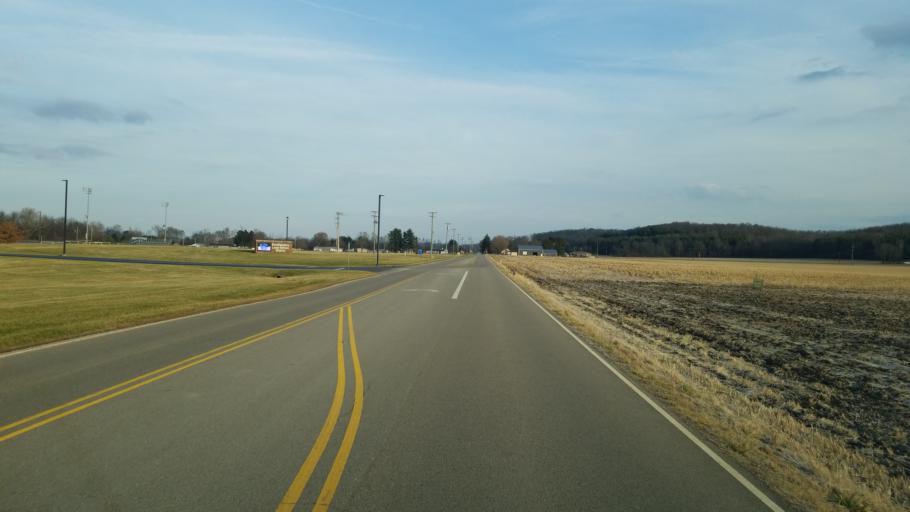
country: US
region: Ohio
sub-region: Ross County
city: Chillicothe
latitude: 39.2809
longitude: -82.8687
